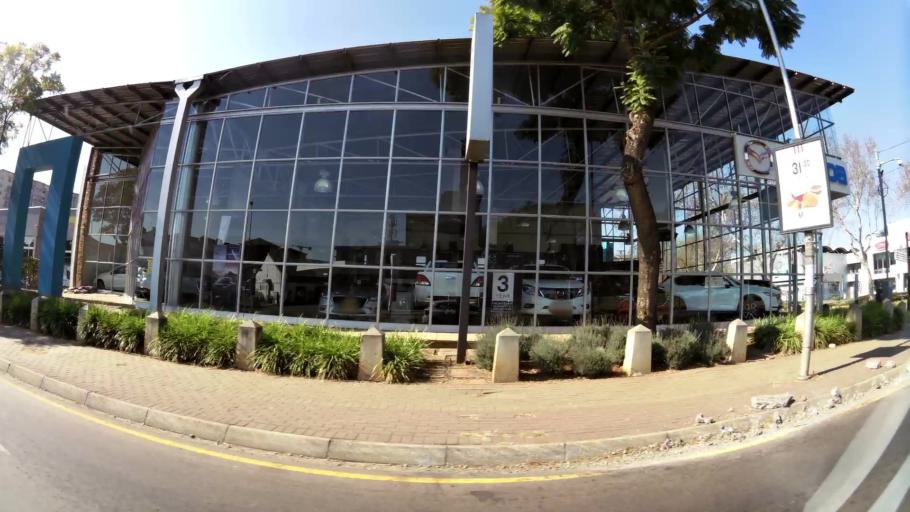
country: ZA
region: Gauteng
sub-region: City of Tshwane Metropolitan Municipality
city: Pretoria
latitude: -25.7501
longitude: 28.2401
